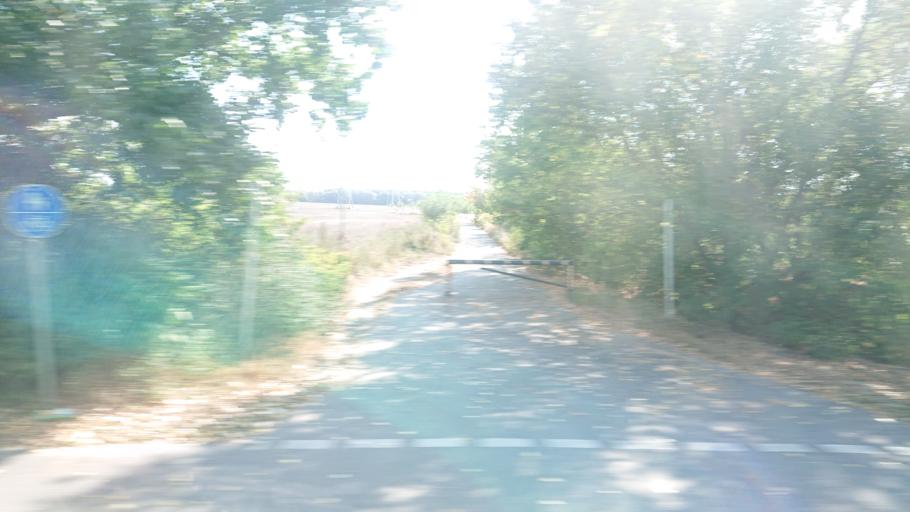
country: DE
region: Berlin
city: Karow
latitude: 52.5940
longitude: 13.4987
